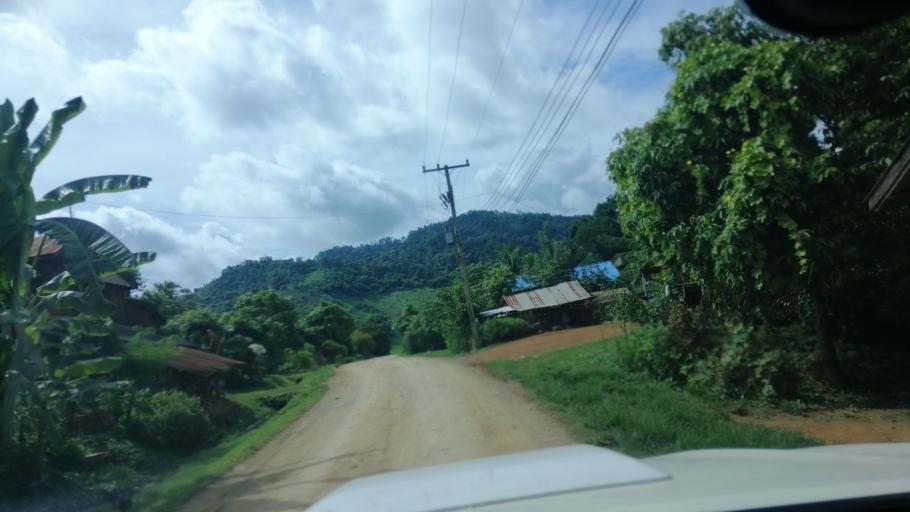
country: TH
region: Phayao
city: Phu Sang
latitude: 19.6120
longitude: 100.5390
